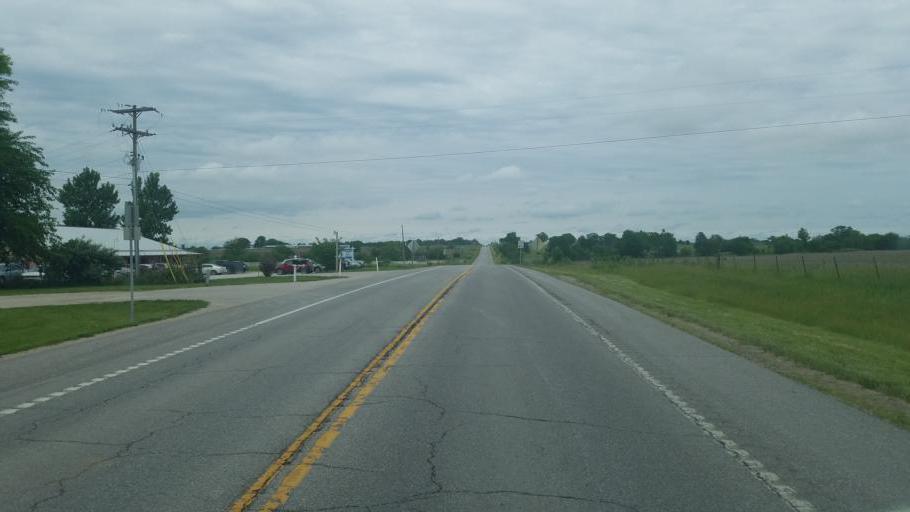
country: US
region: Missouri
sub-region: Morgan County
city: Versailles
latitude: 38.4490
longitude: -92.8093
